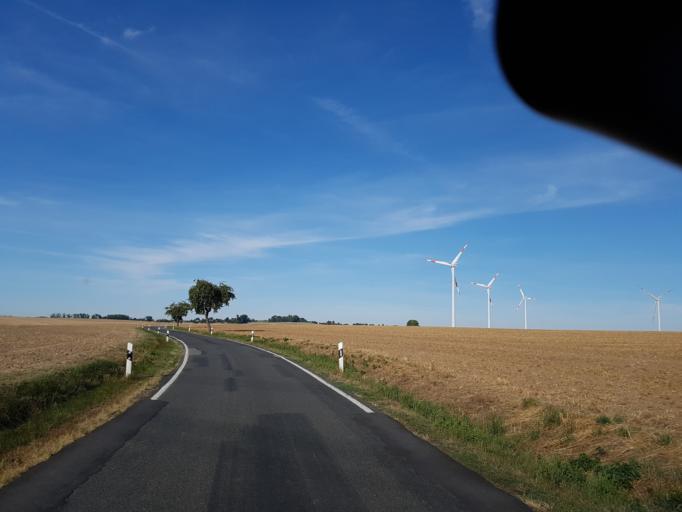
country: DE
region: Saxony
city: Ostrau
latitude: 51.2380
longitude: 13.1604
